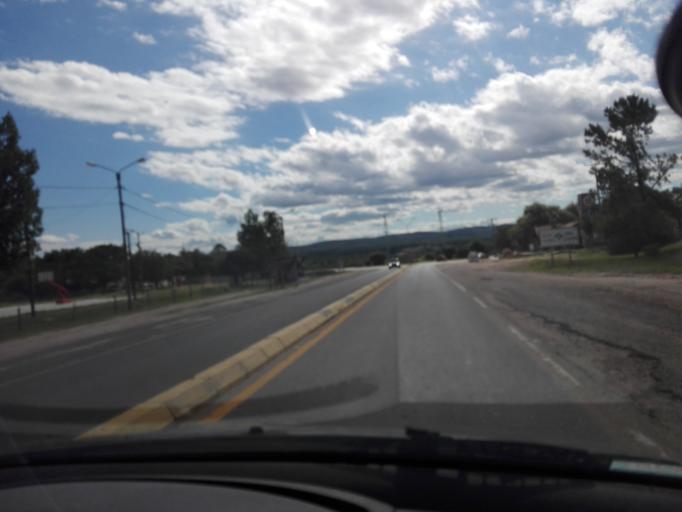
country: AR
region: Cordoba
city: Mina Clavero
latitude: -31.7420
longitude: -65.0036
